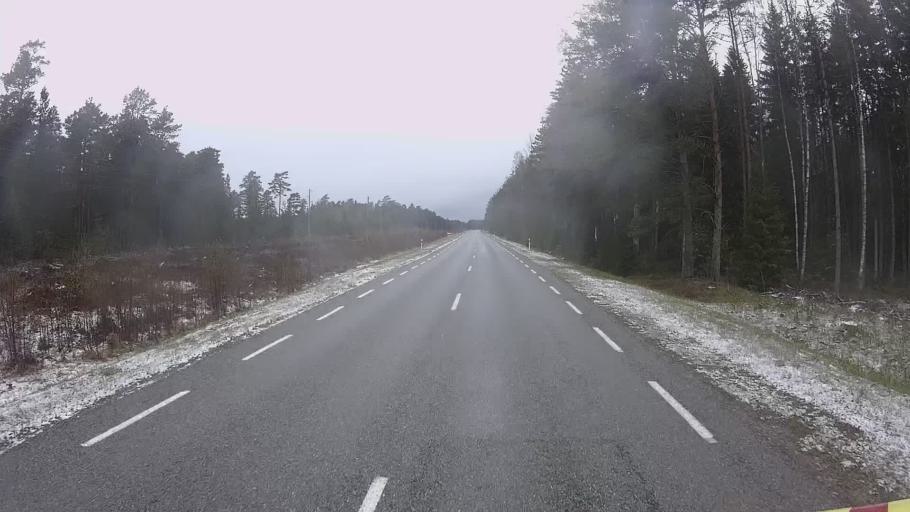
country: EE
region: Hiiumaa
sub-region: Kaerdla linn
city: Kardla
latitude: 59.0179
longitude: 22.6720
